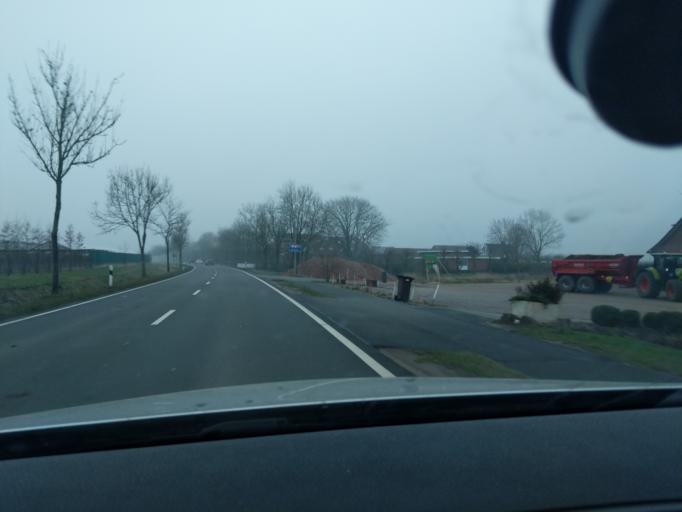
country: DE
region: Lower Saxony
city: Jork
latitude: 53.5493
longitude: 9.6667
